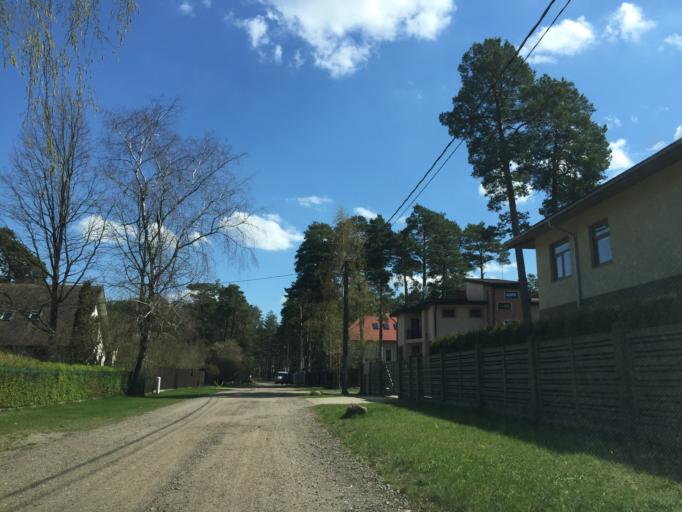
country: LV
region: Saulkrastu
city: Saulkrasti
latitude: 57.2416
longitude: 24.4027
